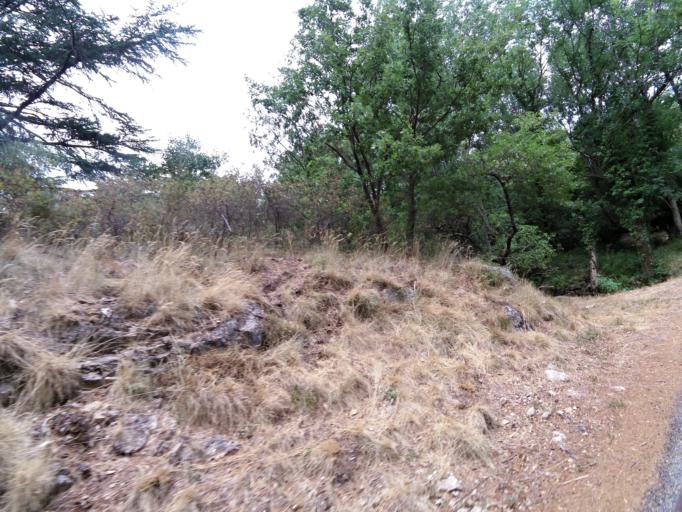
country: FR
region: Languedoc-Roussillon
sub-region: Departement du Gard
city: Le Vigan
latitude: 44.0364
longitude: 3.6088
